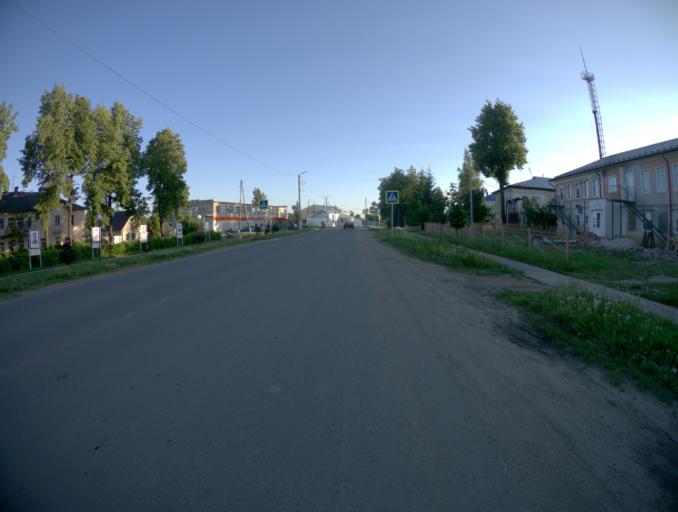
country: RU
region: Ivanovo
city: Gavrilov Posad
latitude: 56.5607
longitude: 40.1238
